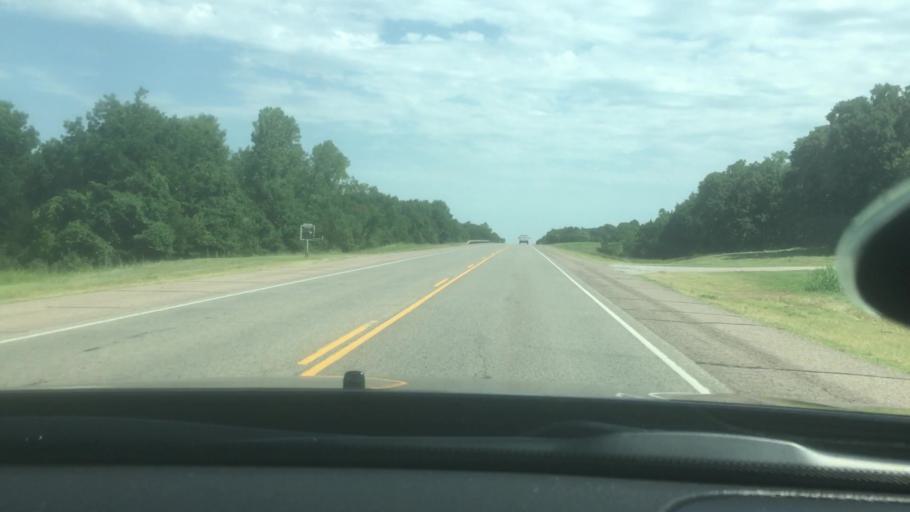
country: US
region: Oklahoma
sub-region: Seminole County
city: Konawa
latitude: 35.0060
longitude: -96.9314
